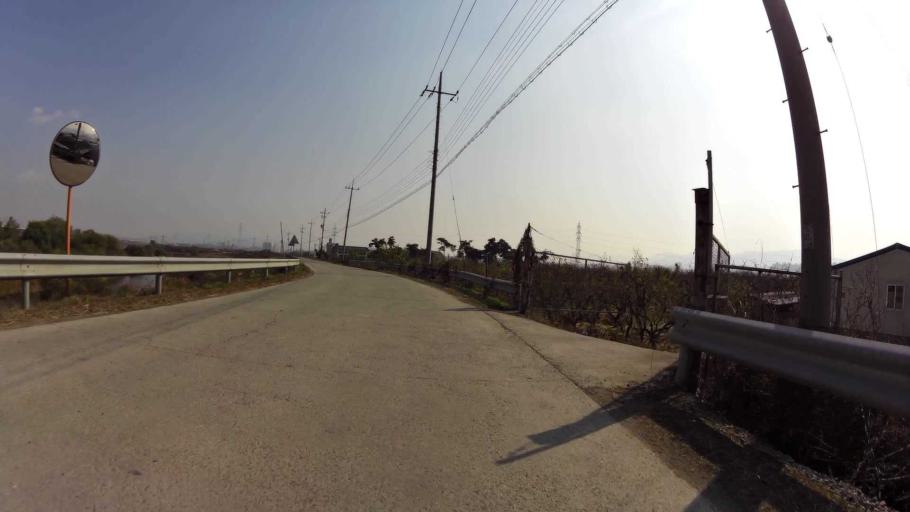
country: KR
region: Gyeongsangbuk-do
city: Gyeongsan-si
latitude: 35.8511
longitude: 128.7342
